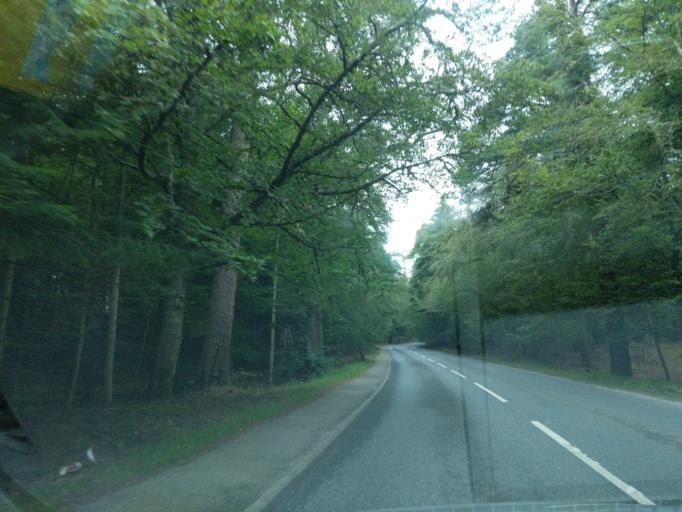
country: GB
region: Scotland
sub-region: Highland
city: Grantown on Spey
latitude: 57.3254
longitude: -3.6065
